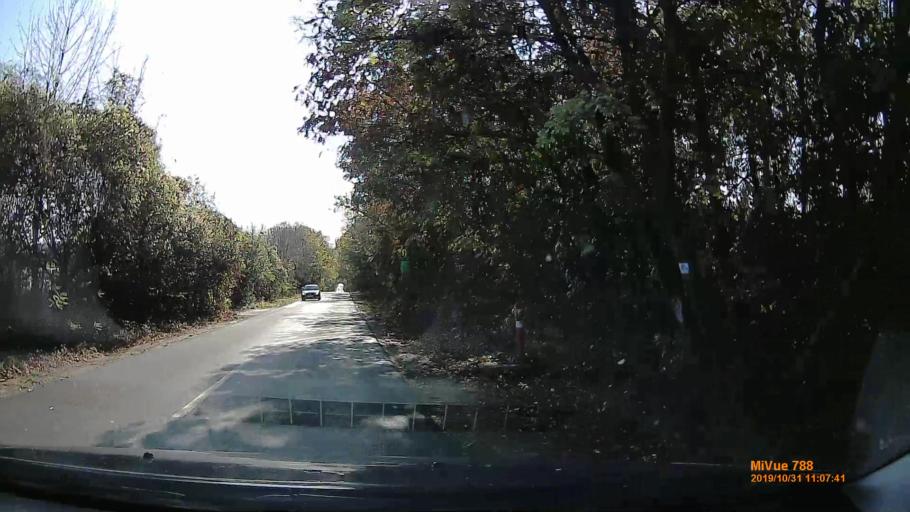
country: HU
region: Pest
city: Pilisborosjeno
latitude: 47.5946
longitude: 19.0010
